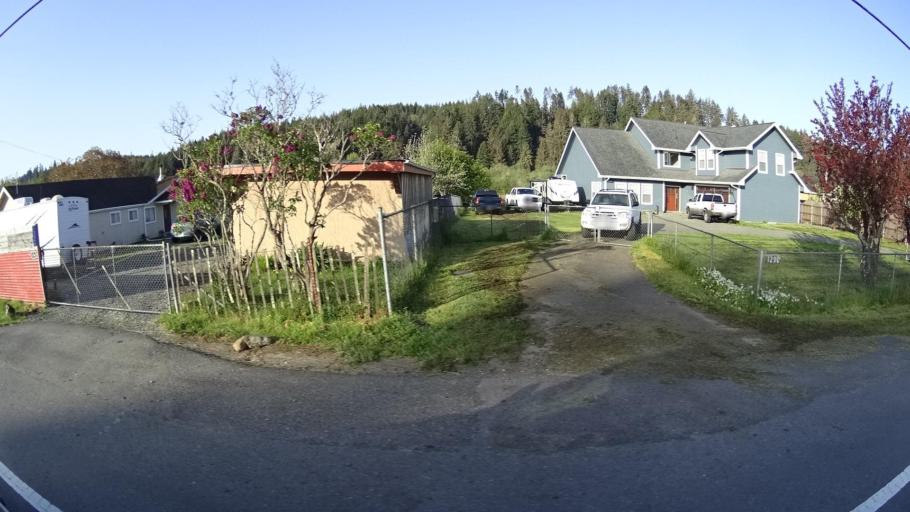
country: US
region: California
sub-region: Humboldt County
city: Myrtletown
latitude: 40.7705
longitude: -124.0730
